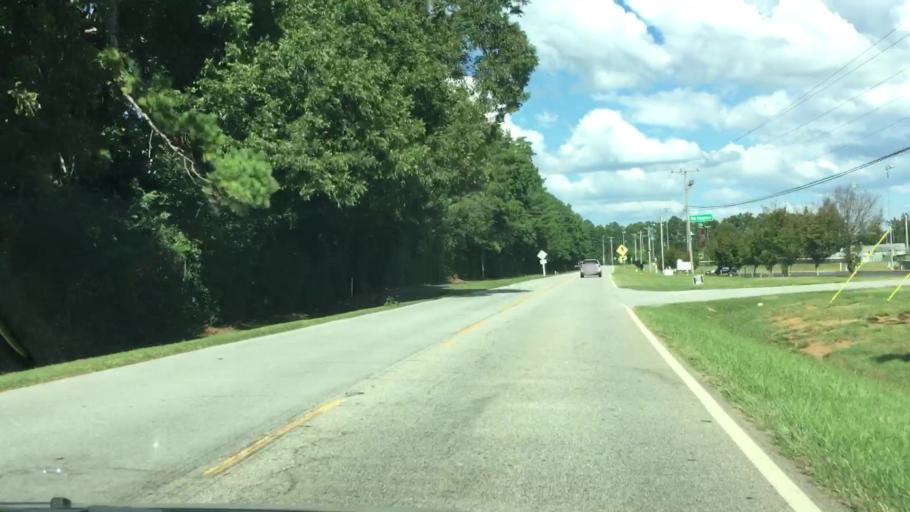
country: US
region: Georgia
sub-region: Fayette County
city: Shannon
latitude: 33.4229
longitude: -84.4710
